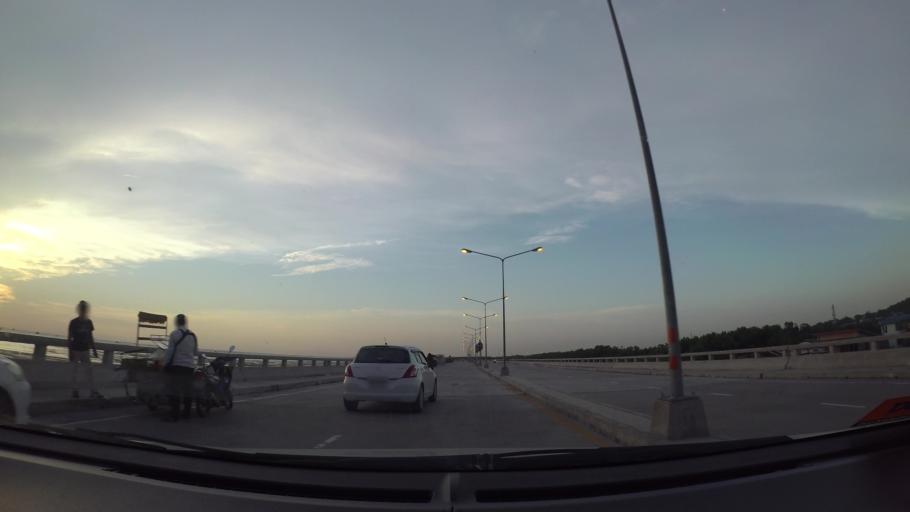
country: TH
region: Chon Buri
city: Chon Buri
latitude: 13.3884
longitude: 100.9825
